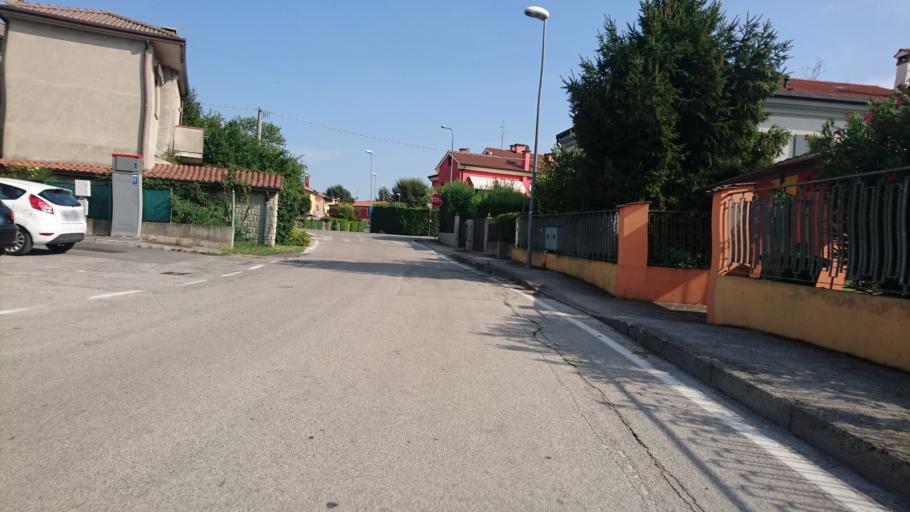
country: IT
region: Veneto
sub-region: Provincia di Padova
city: Selvazzano Dentro
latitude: 45.4002
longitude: 11.7804
